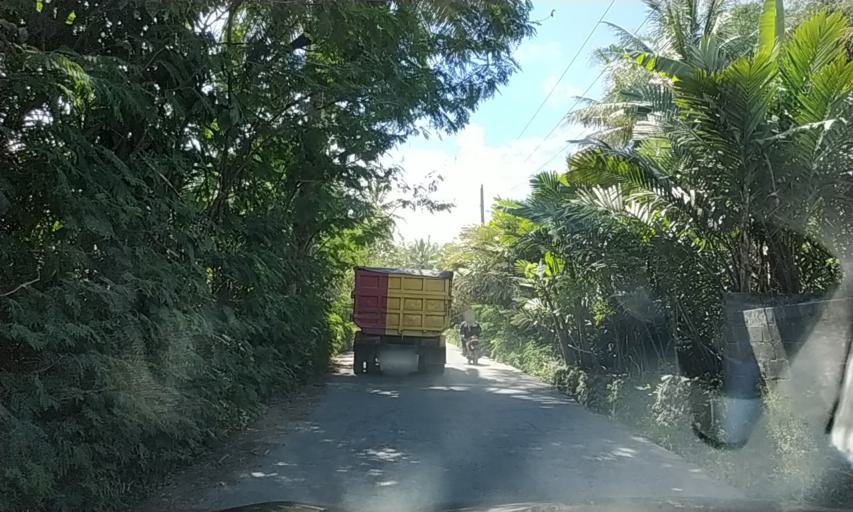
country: ID
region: Central Java
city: Muntilan
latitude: -7.6058
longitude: 110.3618
